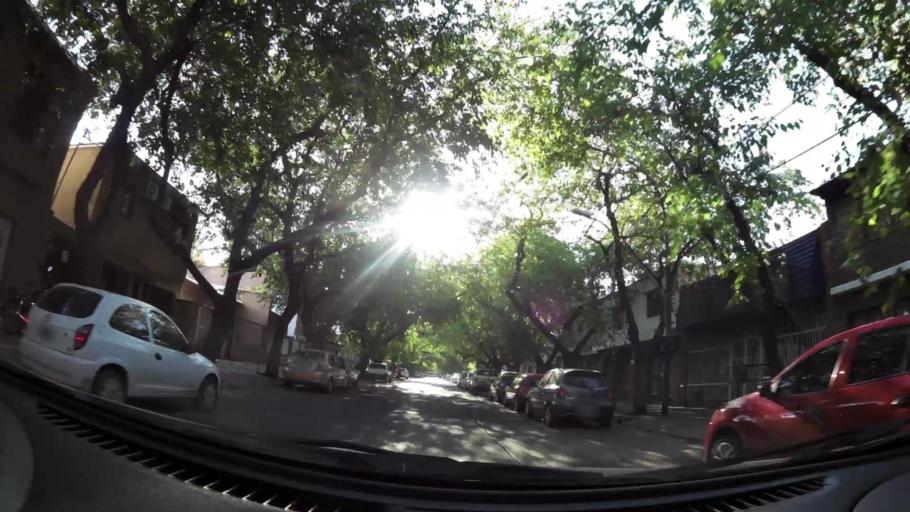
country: AR
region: Mendoza
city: Mendoza
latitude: -32.9031
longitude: -68.8388
